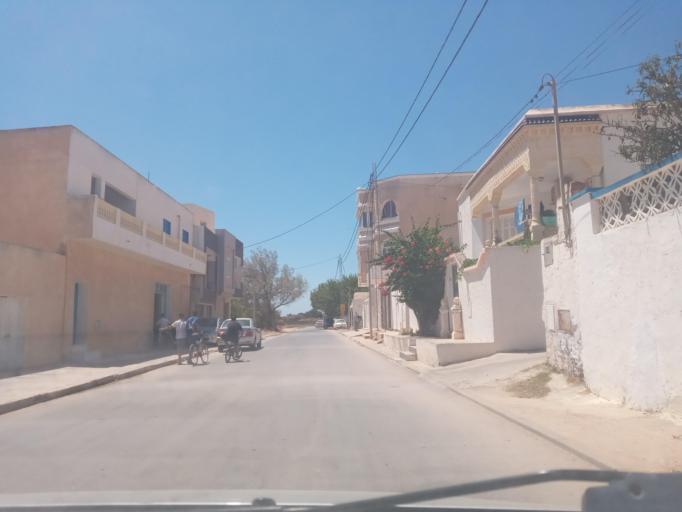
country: TN
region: Nabul
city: El Haouaria
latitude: 37.0488
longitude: 11.0068
